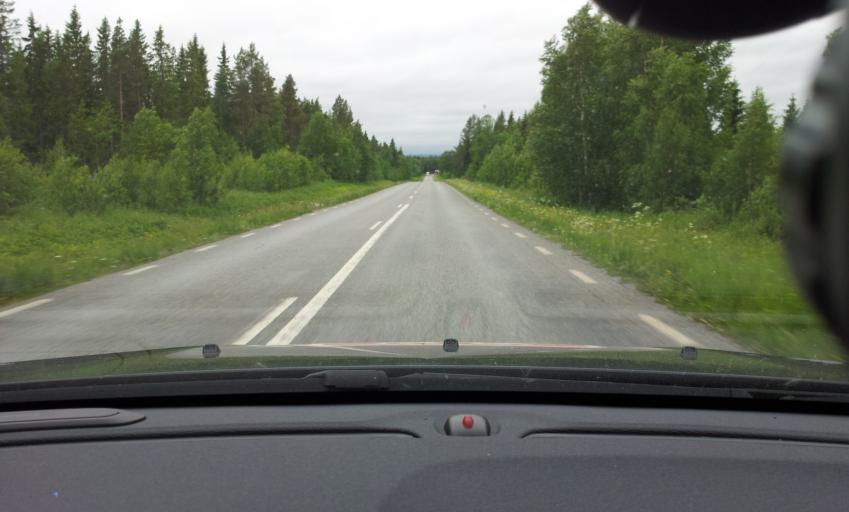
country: SE
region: Jaemtland
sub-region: Krokoms Kommun
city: Krokom
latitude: 63.1312
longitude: 14.2435
